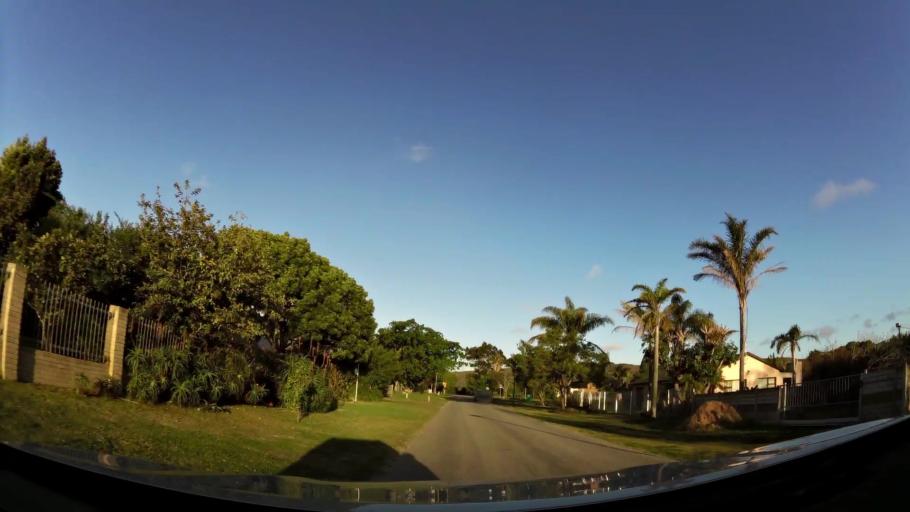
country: ZA
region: Western Cape
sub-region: Eden District Municipality
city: Knysna
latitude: -34.0161
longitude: 22.7849
